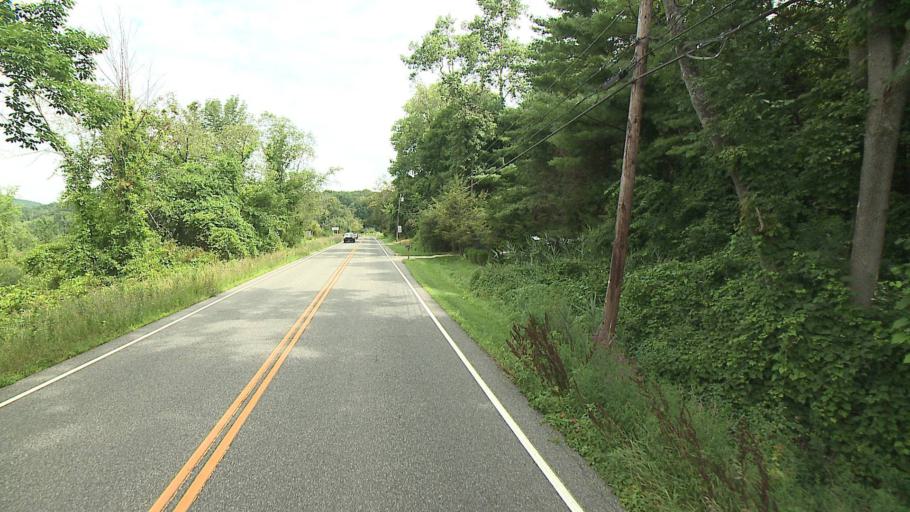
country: US
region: Connecticut
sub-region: Fairfield County
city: Sherman
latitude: 41.6356
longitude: -73.4996
